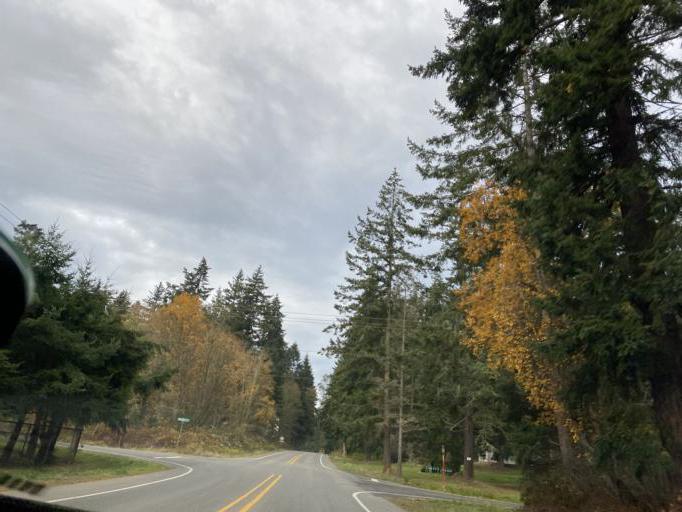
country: US
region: Washington
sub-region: Island County
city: Freeland
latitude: 48.0006
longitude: -122.5363
